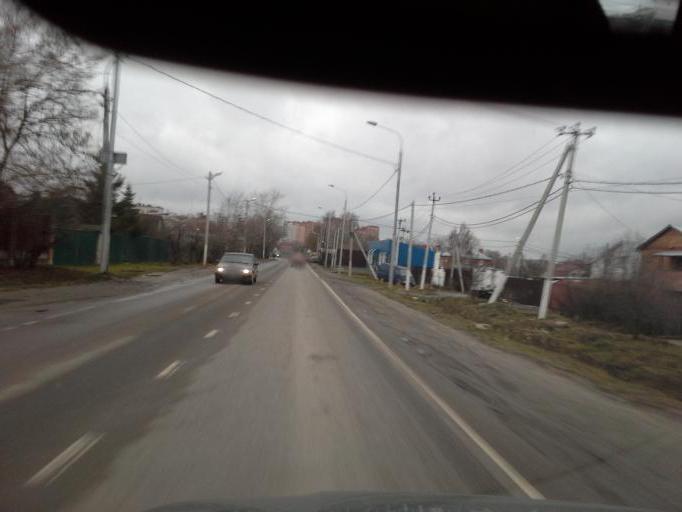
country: RU
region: Moscow
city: Vnukovo
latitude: 55.5956
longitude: 37.2127
